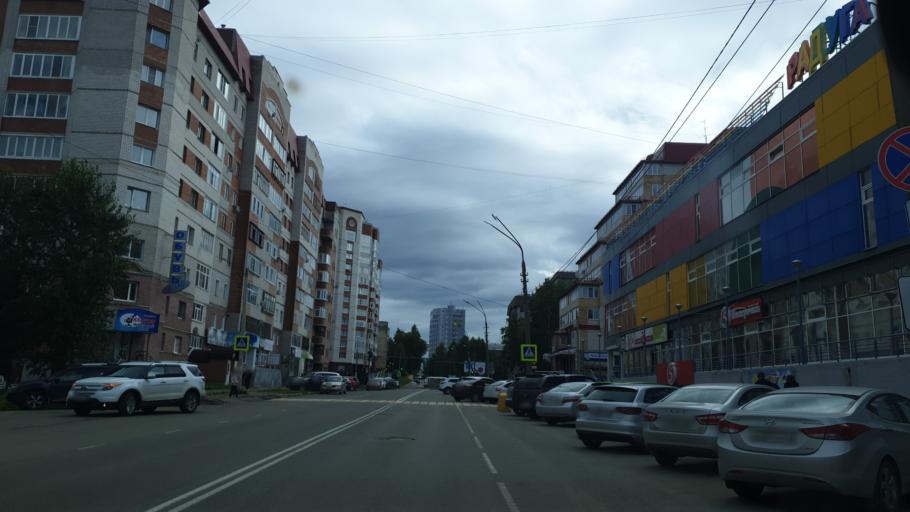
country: RU
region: Komi Republic
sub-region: Syktyvdinskiy Rayon
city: Syktyvkar
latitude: 61.6737
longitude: 50.8246
